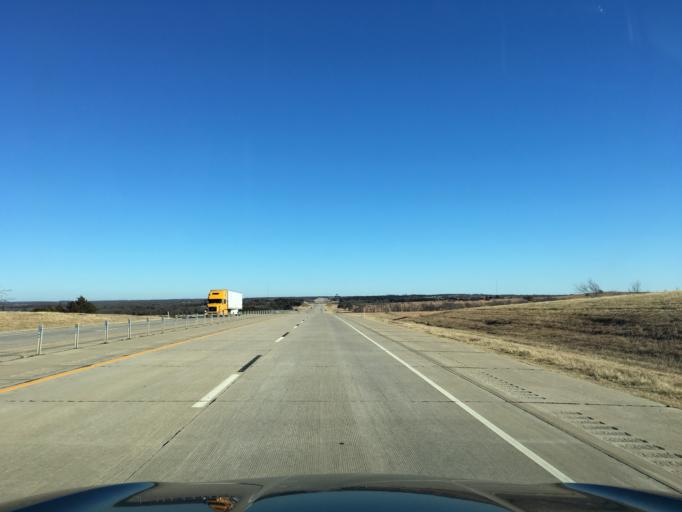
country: US
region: Oklahoma
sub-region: Payne County
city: Yale
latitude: 36.2251
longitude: -96.6388
